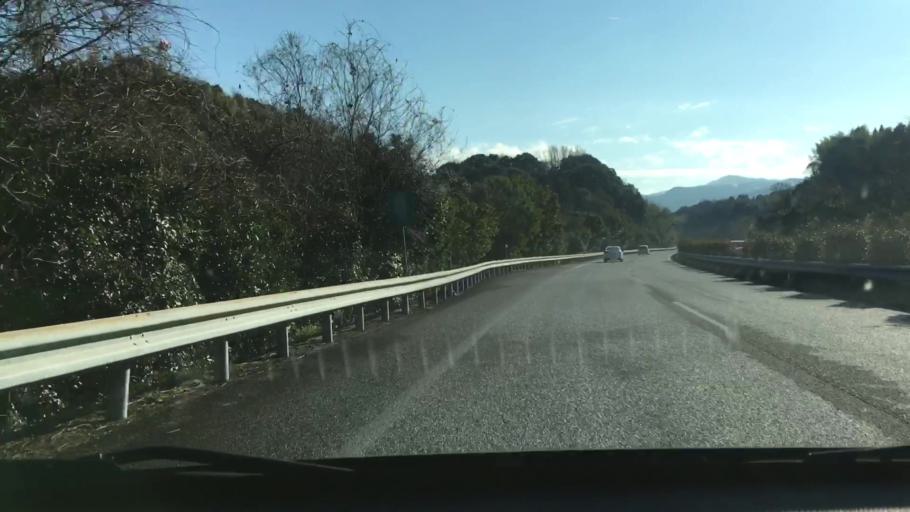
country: JP
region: Kumamoto
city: Hitoyoshi
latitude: 32.1942
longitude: 130.7779
